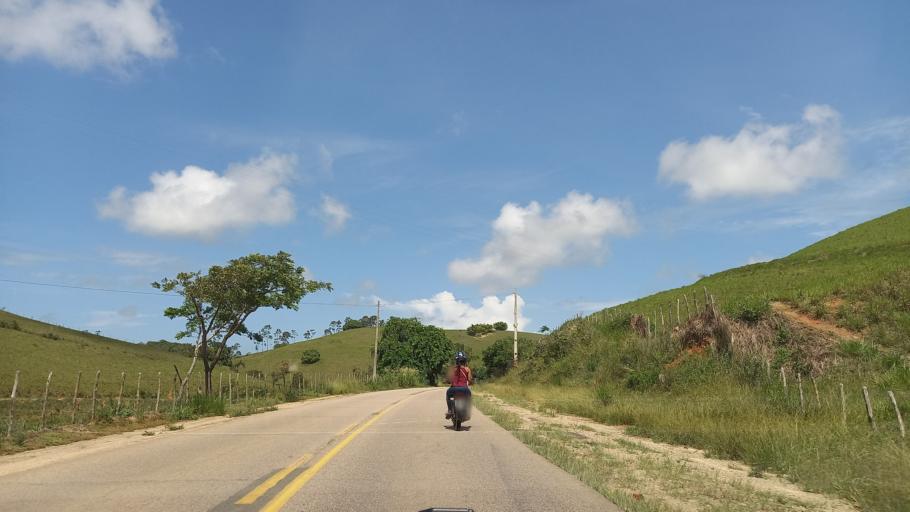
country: BR
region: Pernambuco
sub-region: Tamandare
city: Tamandare
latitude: -8.7454
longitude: -35.1720
